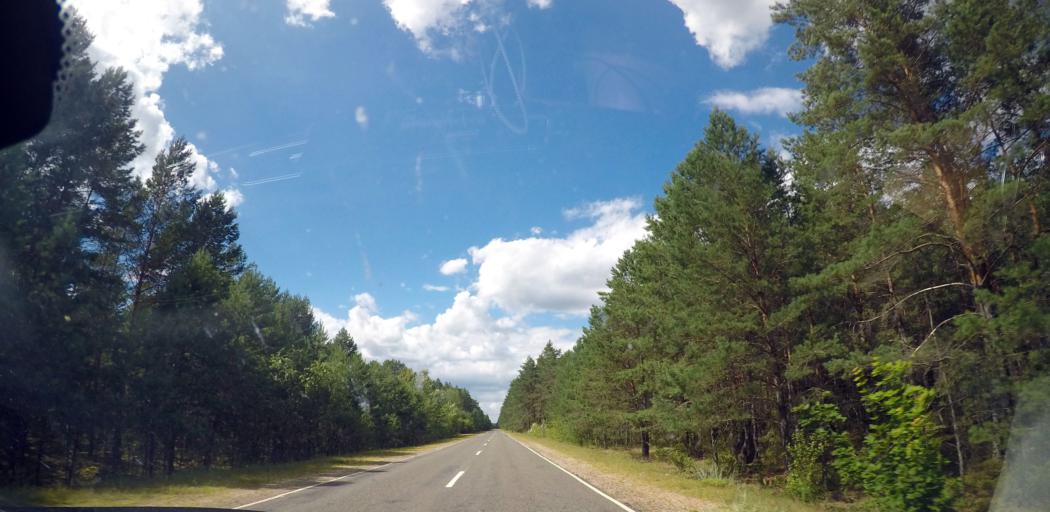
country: LT
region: Alytaus apskritis
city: Druskininkai
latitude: 53.8605
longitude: 24.1786
